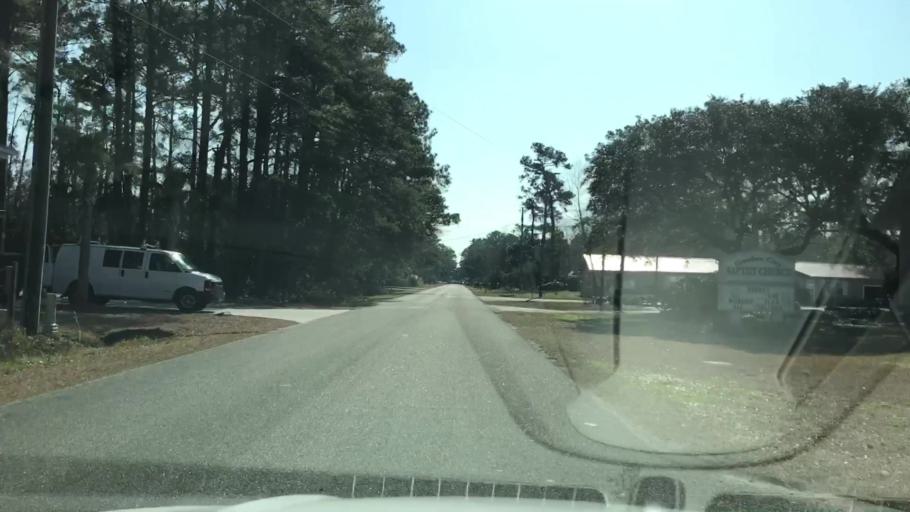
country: US
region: South Carolina
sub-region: Horry County
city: Garden City
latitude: 33.5867
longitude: -79.0051
